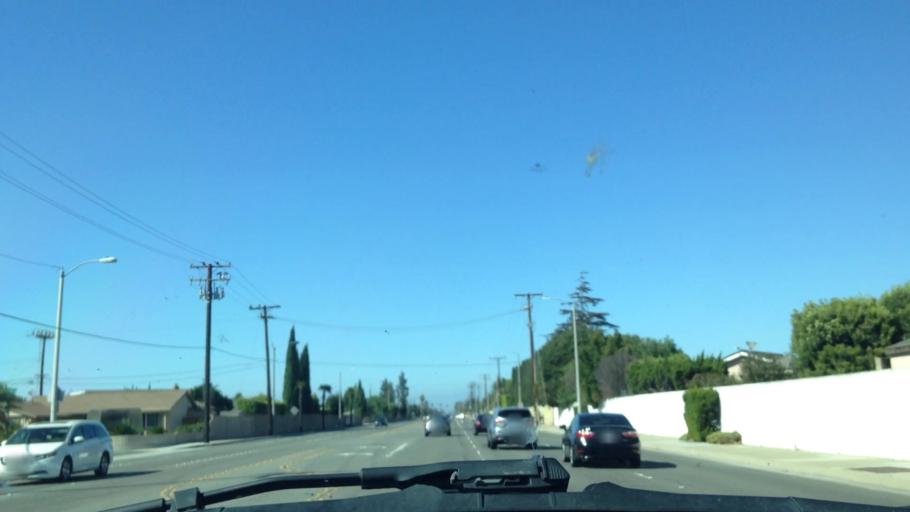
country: US
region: California
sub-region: Orange County
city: Fountain Valley
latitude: 33.7259
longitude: -117.9720
